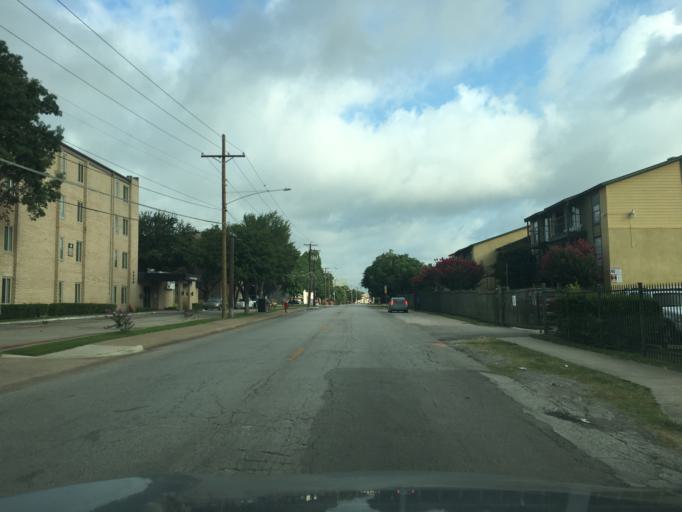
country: US
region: Texas
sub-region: Dallas County
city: University Park
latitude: 32.8685
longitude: -96.7569
